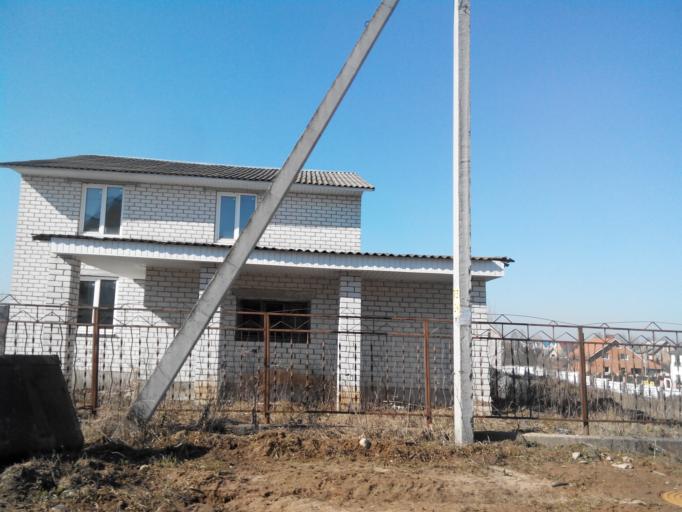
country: BY
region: Minsk
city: Zhdanovichy
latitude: 53.9161
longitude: 27.4018
